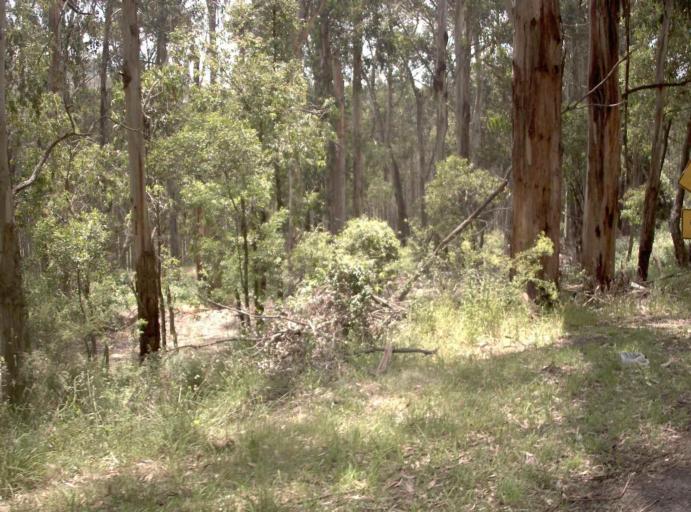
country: AU
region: Victoria
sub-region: Latrobe
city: Traralgon
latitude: -38.3585
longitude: 146.7474
